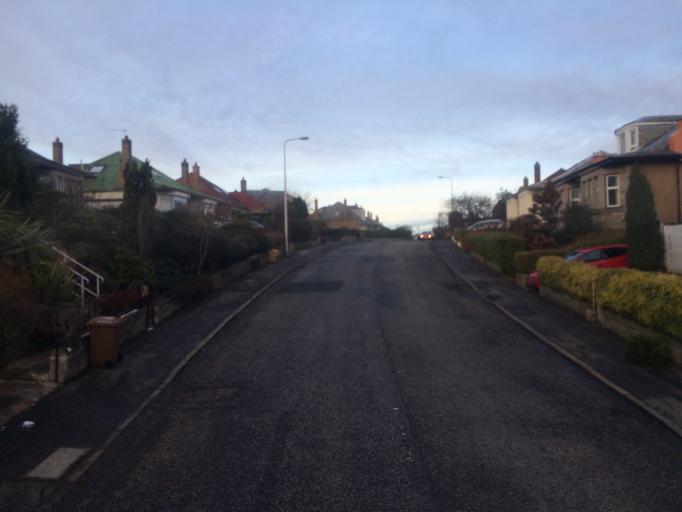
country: GB
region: Scotland
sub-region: Edinburgh
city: Colinton
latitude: 55.9126
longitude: -3.2184
